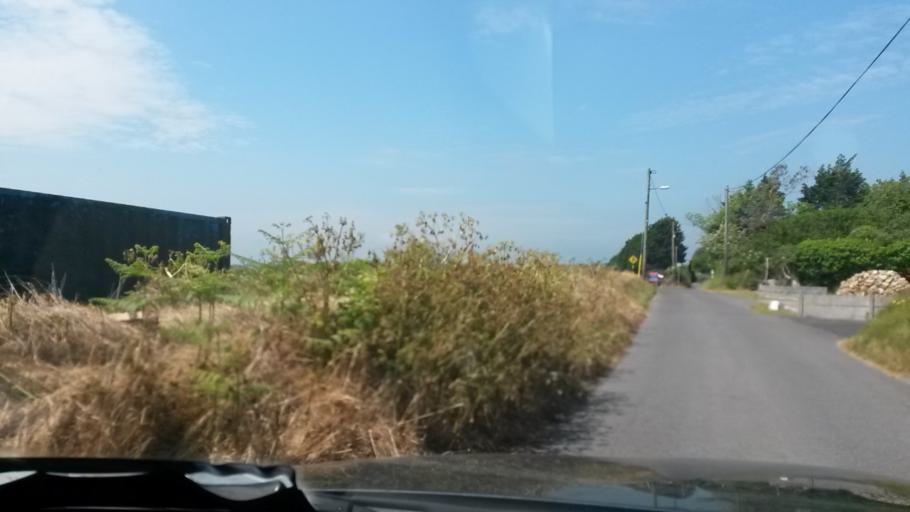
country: IE
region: Leinster
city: Portraine
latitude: 53.5042
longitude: -6.1230
